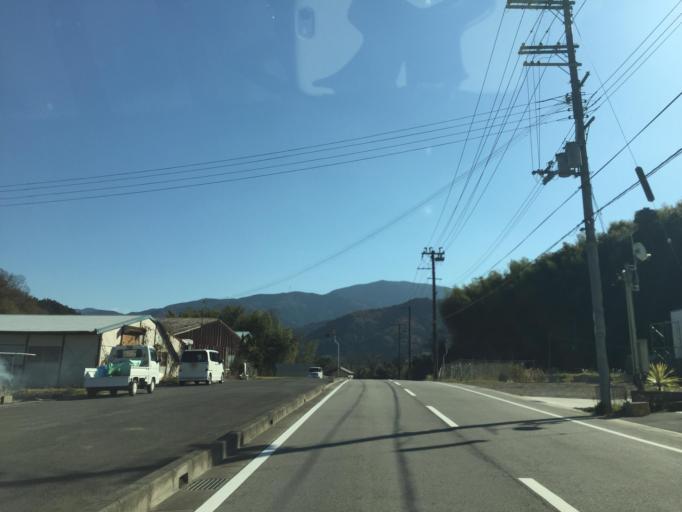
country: JP
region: Wakayama
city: Iwade
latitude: 34.1514
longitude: 135.3450
